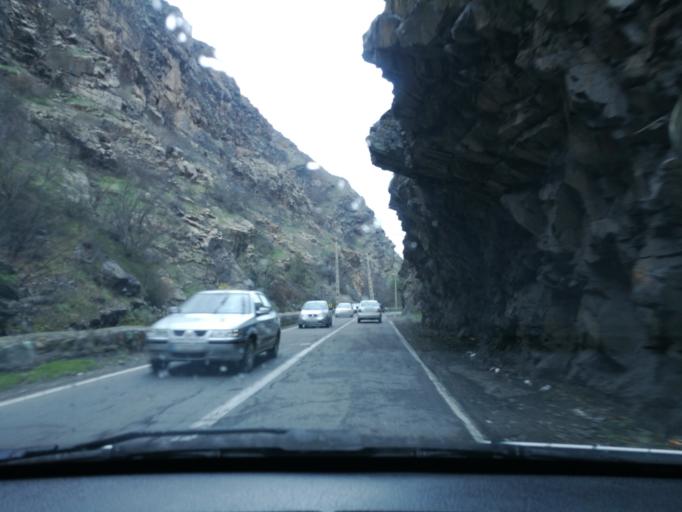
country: IR
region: Mazandaran
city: Chalus
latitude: 36.2952
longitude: 51.2459
